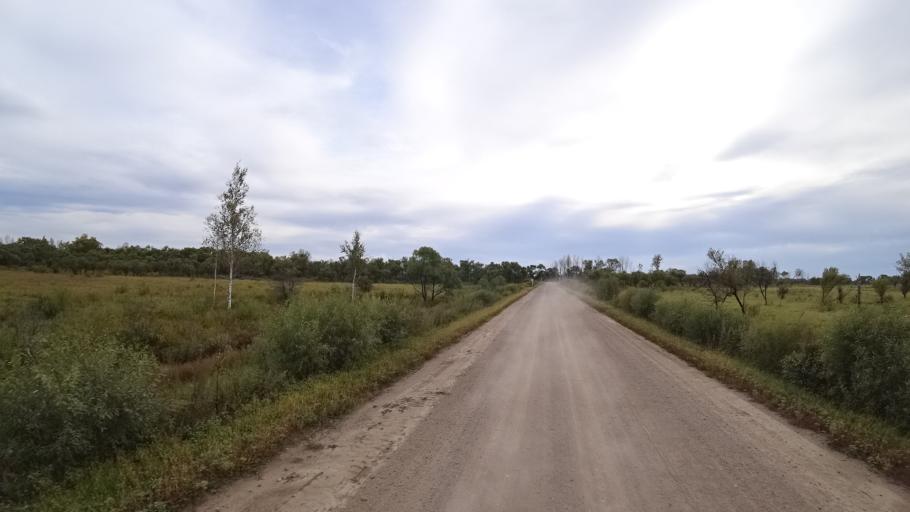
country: RU
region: Amur
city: Arkhara
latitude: 49.3747
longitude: 130.2071
